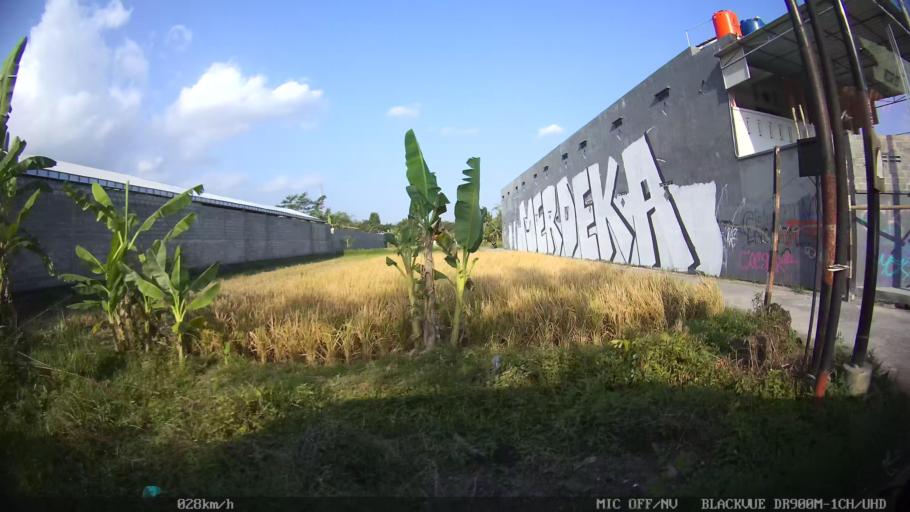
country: ID
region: Daerah Istimewa Yogyakarta
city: Gamping Lor
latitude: -7.7934
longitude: 110.3334
